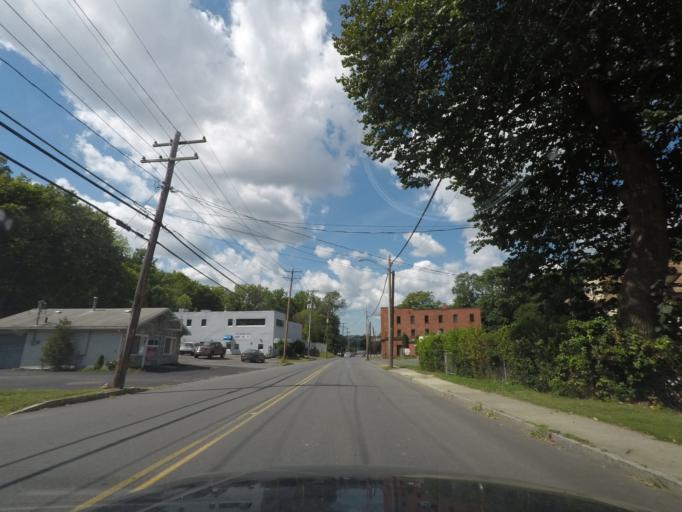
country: US
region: New York
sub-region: Rensselaer County
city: Troy
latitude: 42.7185
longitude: -73.6824
